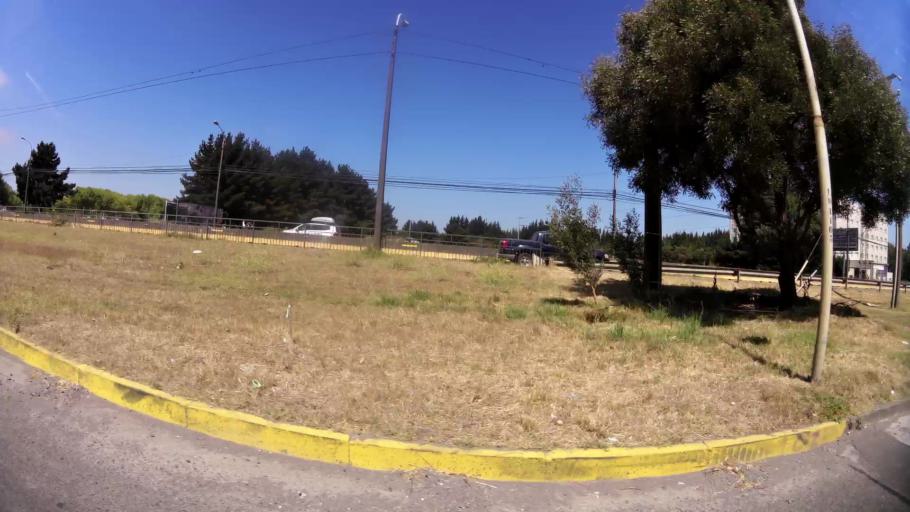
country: CL
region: Biobio
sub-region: Provincia de Concepcion
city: Concepcion
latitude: -36.7999
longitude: -73.0702
